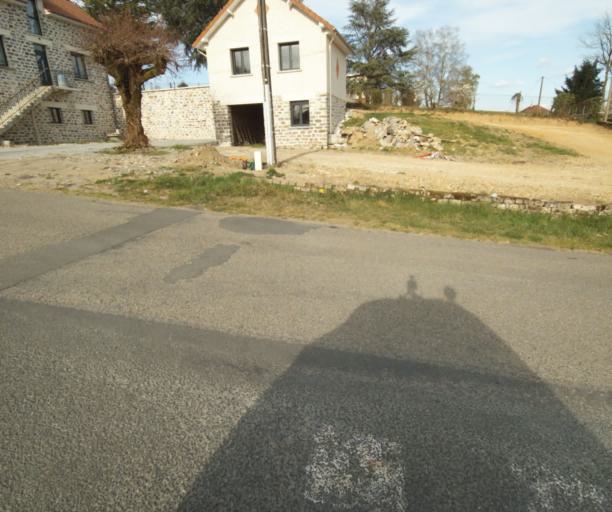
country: FR
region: Limousin
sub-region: Departement de la Correze
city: Naves
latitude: 45.3189
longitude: 1.7629
